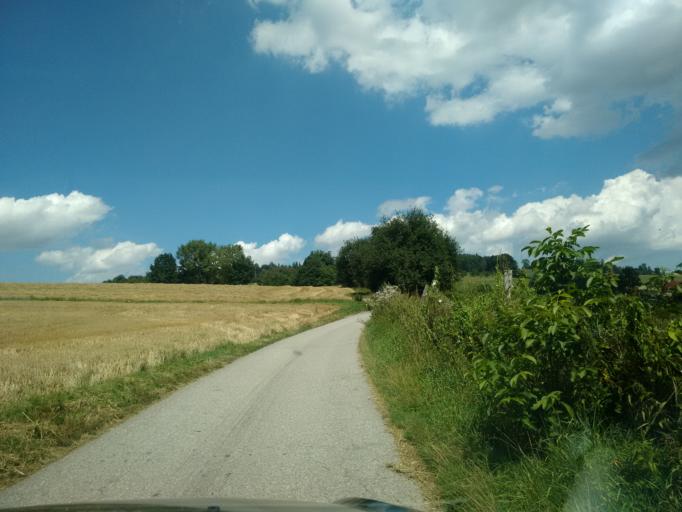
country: AT
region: Upper Austria
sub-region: Wels-Land
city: Gunskirchen
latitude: 48.1761
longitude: 13.9483
